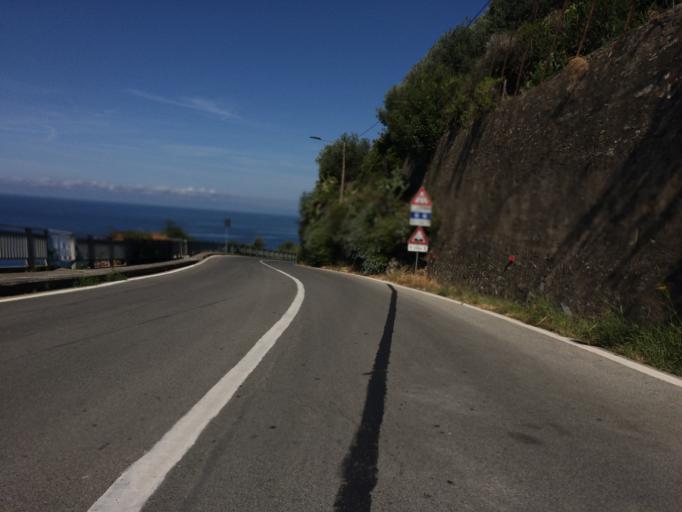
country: IT
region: Liguria
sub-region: Provincia di Genova
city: Camogli
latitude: 44.3565
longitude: 9.1527
